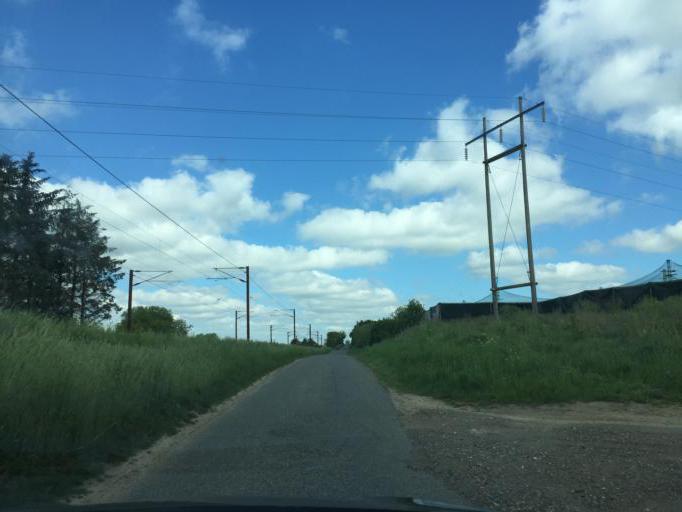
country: DK
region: South Denmark
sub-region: Assens Kommune
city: Tommerup
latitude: 55.3442
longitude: 10.2092
